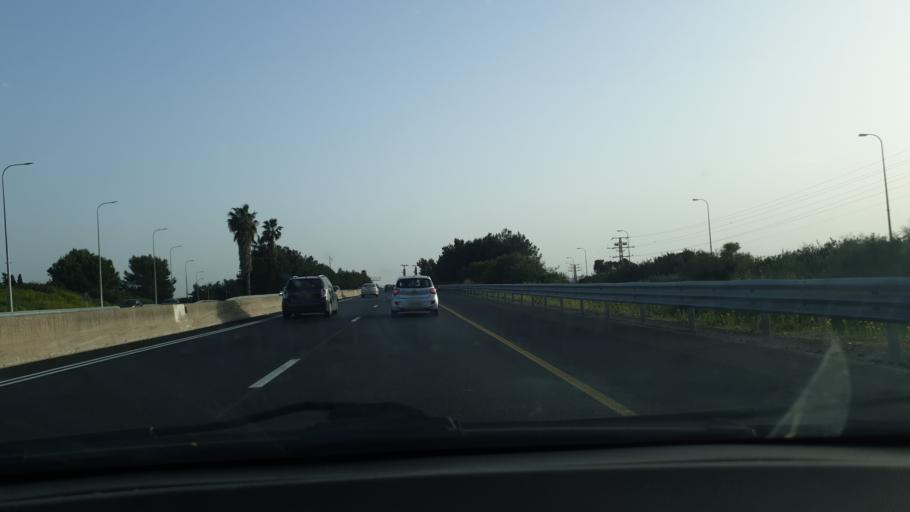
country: IL
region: Central District
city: Even Yehuda
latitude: 32.2375
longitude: 34.8859
